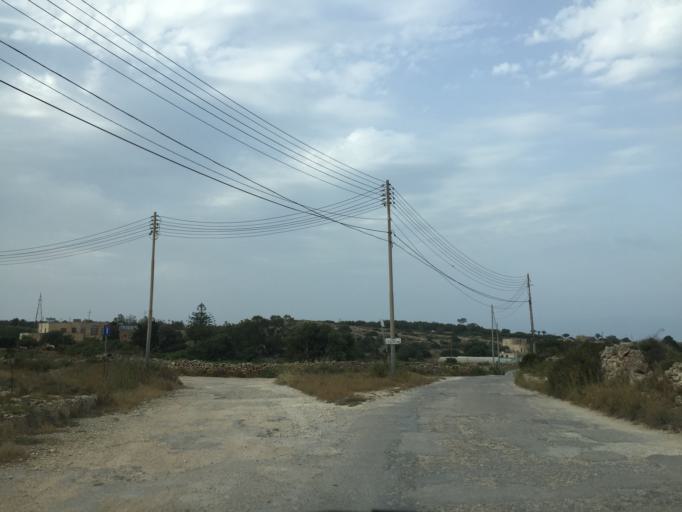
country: MT
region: L-Imgarr
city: Imgarr
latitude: 35.9323
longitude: 14.3869
